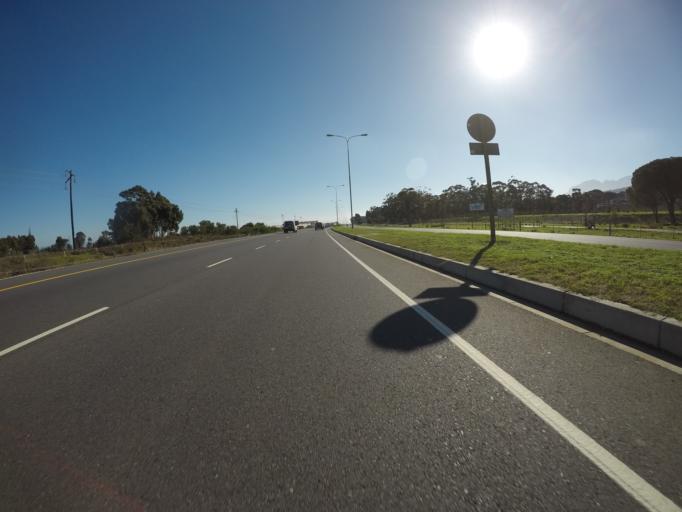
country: ZA
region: Western Cape
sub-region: Overberg District Municipality
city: Grabouw
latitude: -34.1224
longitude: 18.8846
